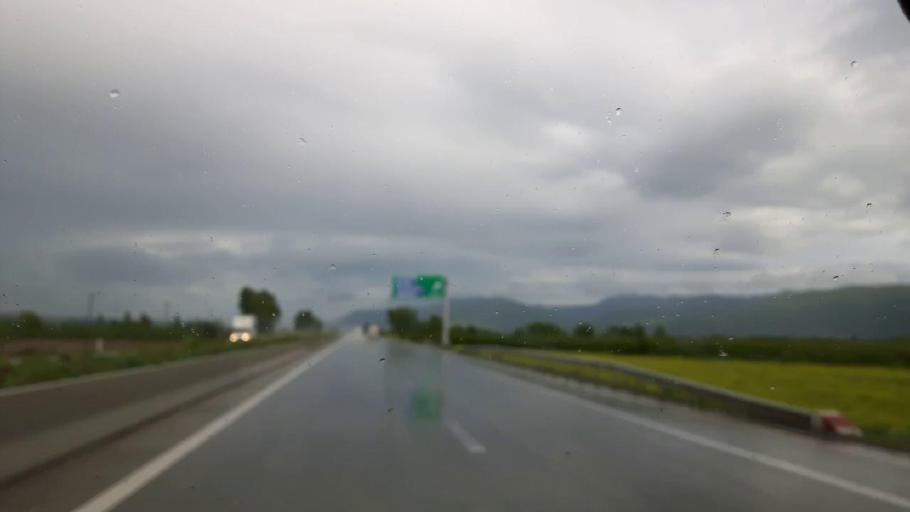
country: GE
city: Agara
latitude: 42.0381
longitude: 43.9352
